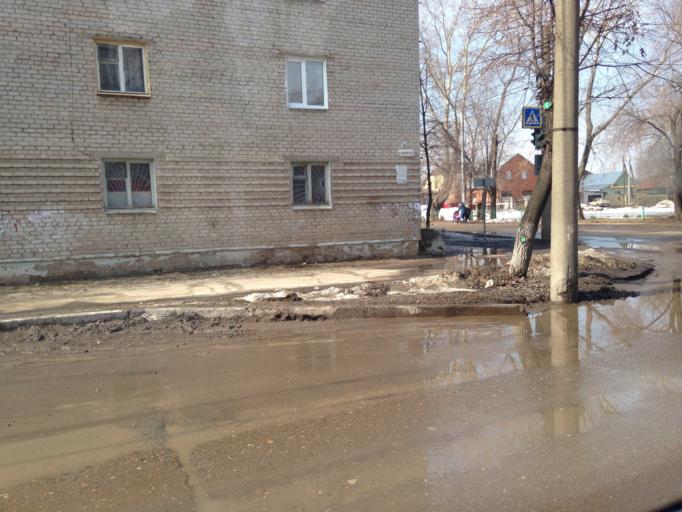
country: RU
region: Ulyanovsk
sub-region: Ulyanovskiy Rayon
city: Ulyanovsk
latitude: 54.3504
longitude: 48.5481
